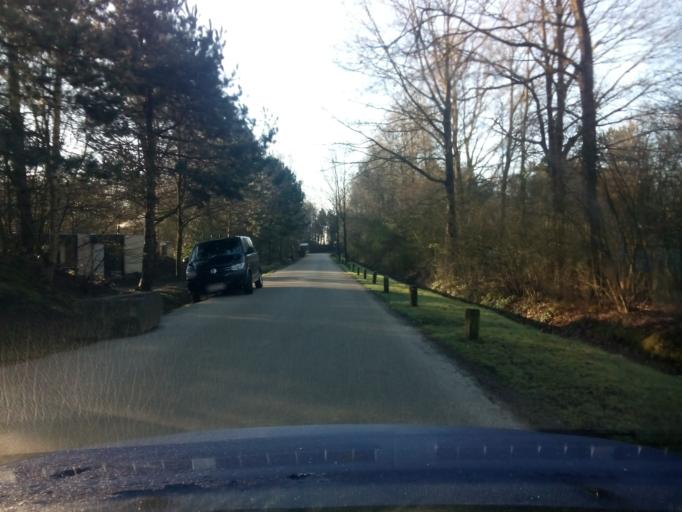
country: NL
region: Drenthe
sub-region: Gemeente Coevorden
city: Dalen
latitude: 52.6743
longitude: 6.7780
